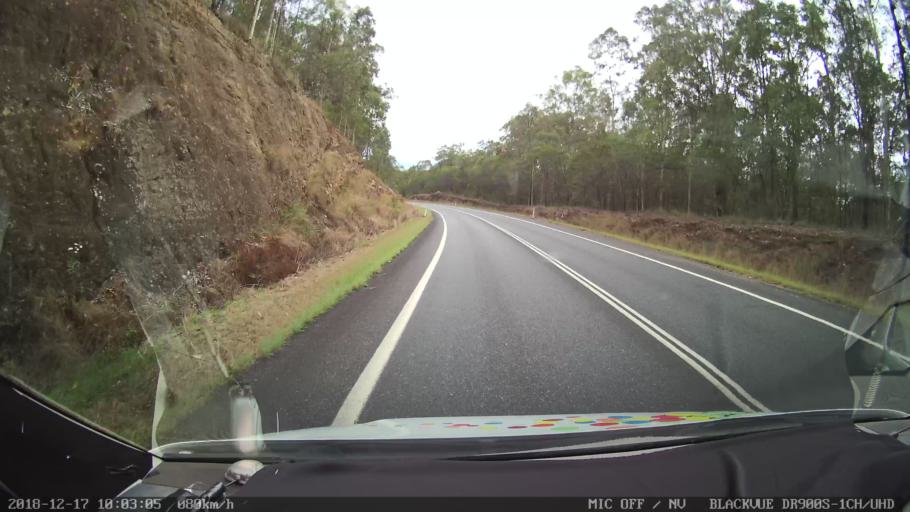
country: AU
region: New South Wales
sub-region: Tenterfield Municipality
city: Carrolls Creek
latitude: -28.8994
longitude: 152.4592
